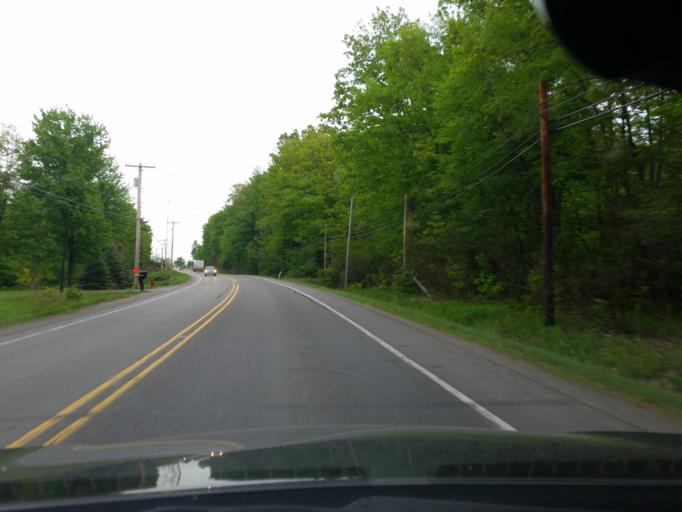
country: US
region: Pennsylvania
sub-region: Elk County
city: Ridgway
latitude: 41.3876
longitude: -78.6905
